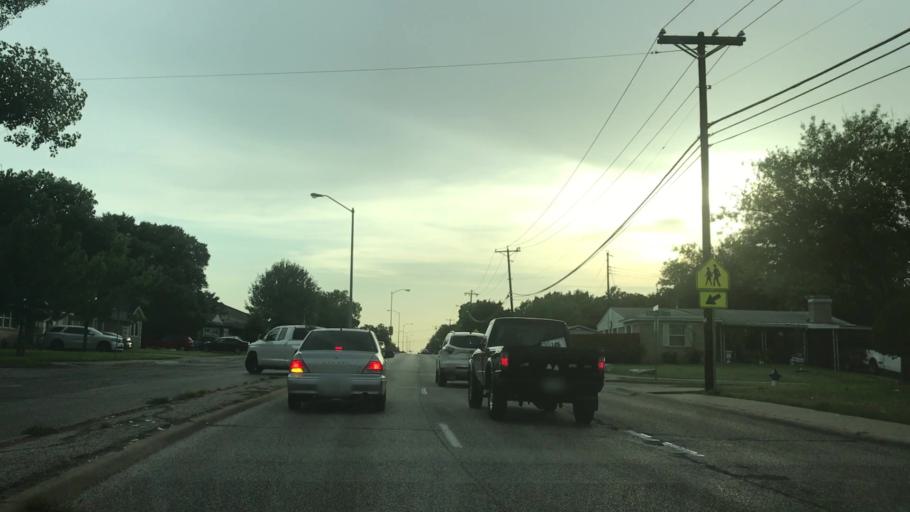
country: US
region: Texas
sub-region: Dallas County
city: Mesquite
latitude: 32.8215
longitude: -96.6500
